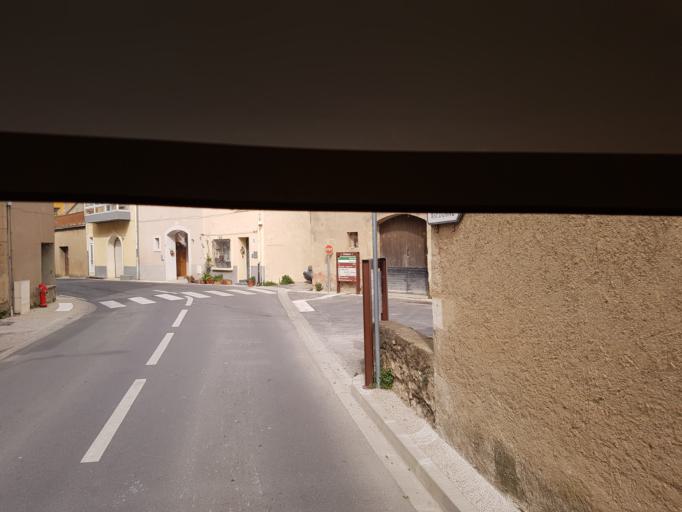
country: FR
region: Languedoc-Roussillon
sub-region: Departement de l'Herault
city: Lespignan
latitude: 43.2715
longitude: 3.1717
